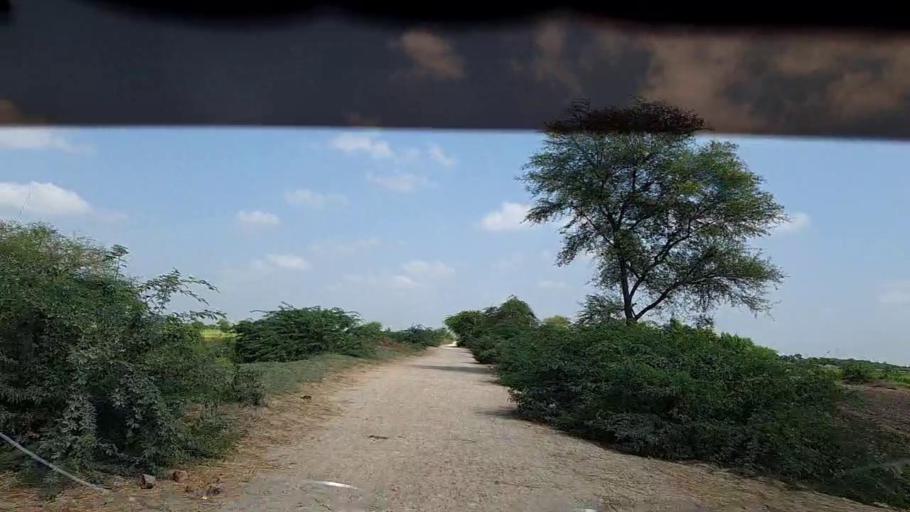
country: PK
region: Sindh
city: Kadhan
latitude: 24.6032
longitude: 68.9796
